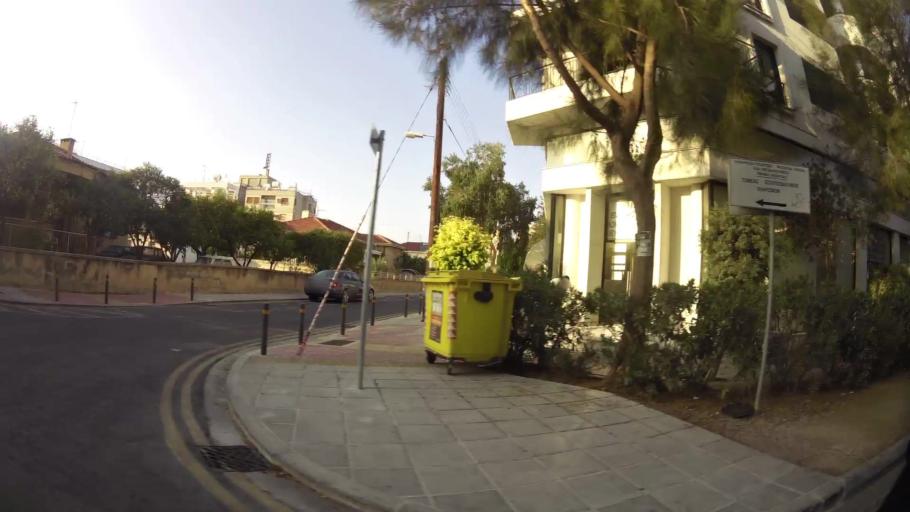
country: CY
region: Lefkosia
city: Nicosia
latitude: 35.1714
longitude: 33.3431
